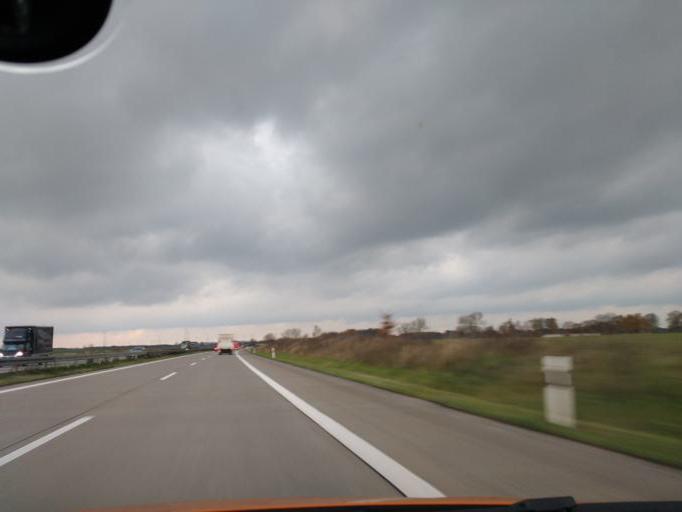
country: DE
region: Brandenburg
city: Heiligengrabe
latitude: 53.1864
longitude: 12.2890
